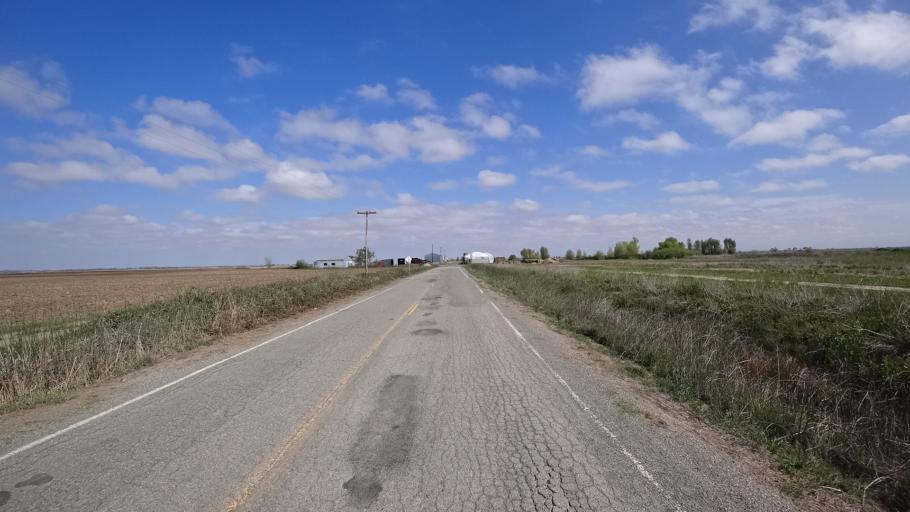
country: US
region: California
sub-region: Colusa County
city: Colusa
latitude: 39.3633
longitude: -121.9363
